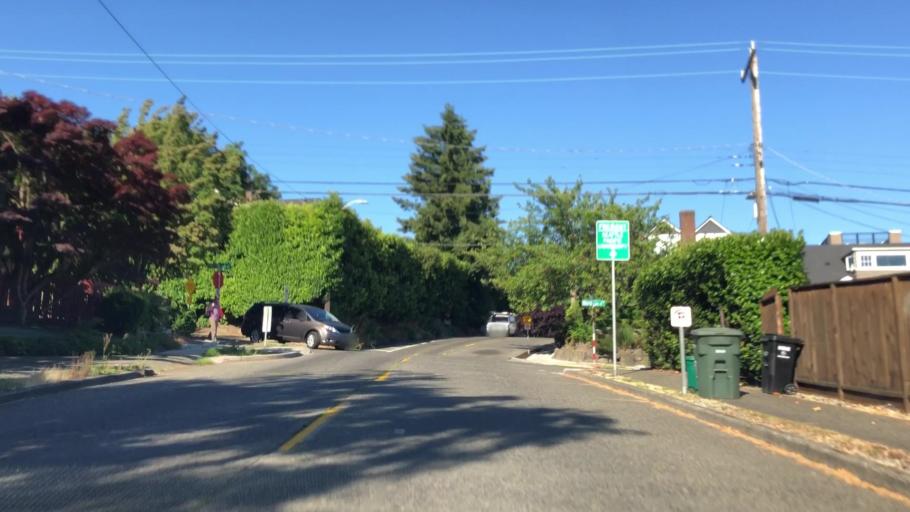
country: US
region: Washington
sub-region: King County
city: Seattle
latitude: 47.6419
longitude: -122.3541
